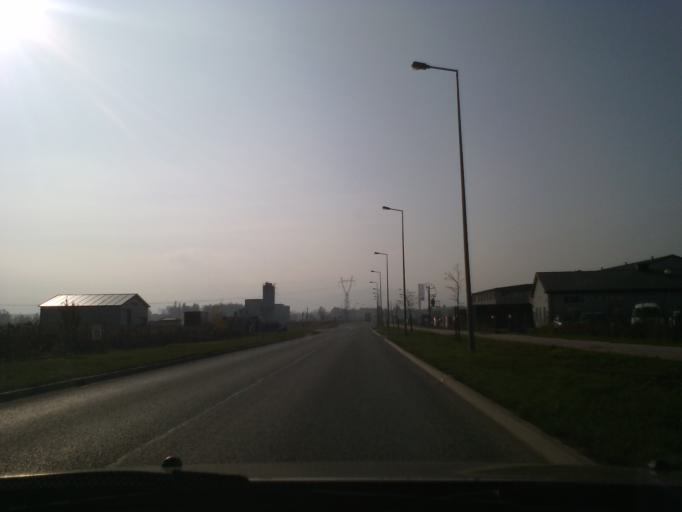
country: PL
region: Lower Silesian Voivodeship
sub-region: Jelenia Gora
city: Cieplice Slaskie Zdroj
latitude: 50.8840
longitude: 15.6983
